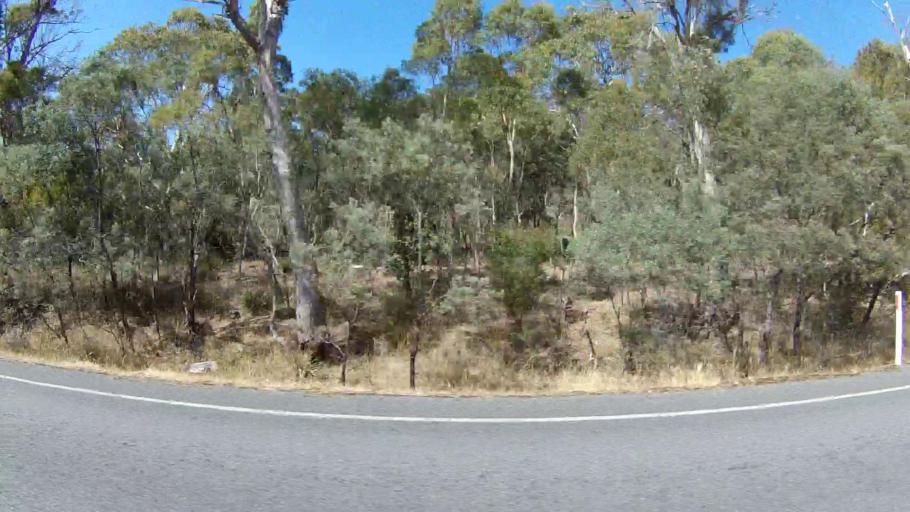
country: AU
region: Tasmania
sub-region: Sorell
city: Sorell
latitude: -42.6076
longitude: 147.6708
